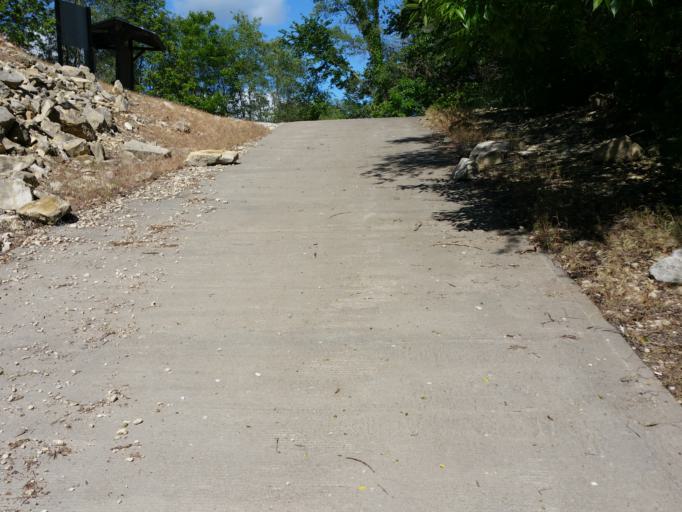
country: US
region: Kansas
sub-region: Riley County
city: Manhattan
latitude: 39.2387
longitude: -96.5858
